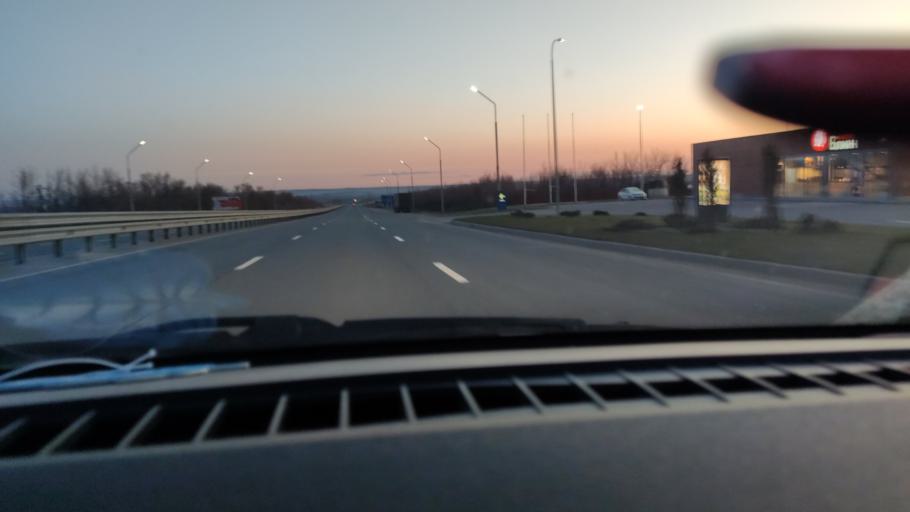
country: RU
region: Saratov
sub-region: Saratovskiy Rayon
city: Saratov
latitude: 51.6582
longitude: 45.9986
